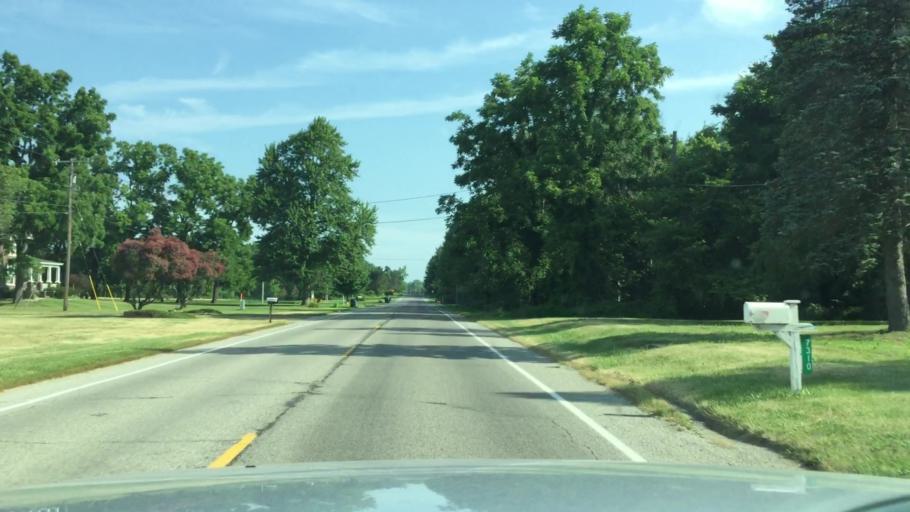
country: US
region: Michigan
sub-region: Genesee County
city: Flushing
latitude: 43.1113
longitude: -83.8728
